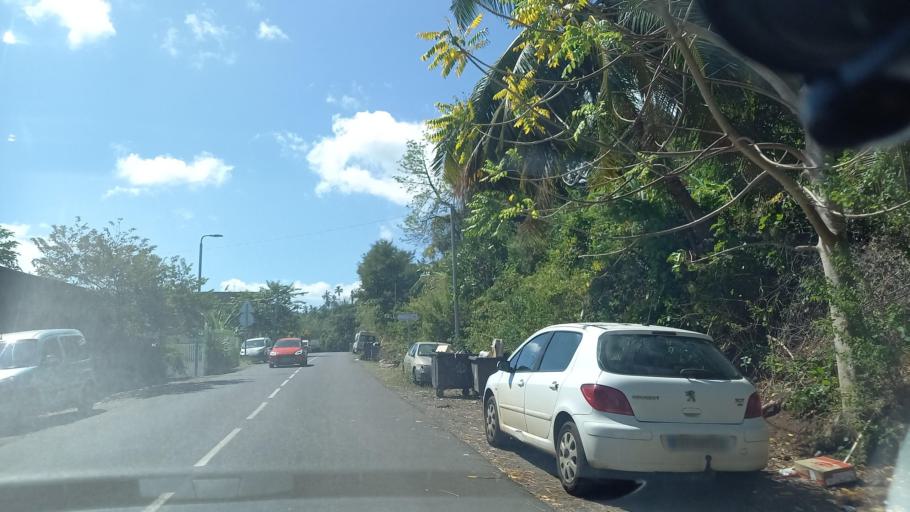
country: YT
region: Kani-Keli
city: Kani Keli
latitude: -12.9452
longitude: 45.1019
